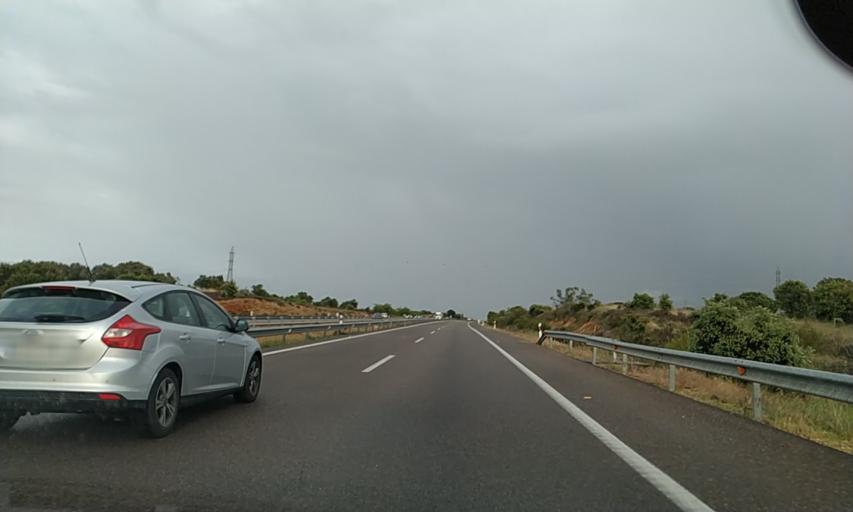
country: ES
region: Extremadura
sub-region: Provincia de Badajoz
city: Talavera La Real
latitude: 38.8721
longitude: -6.8637
